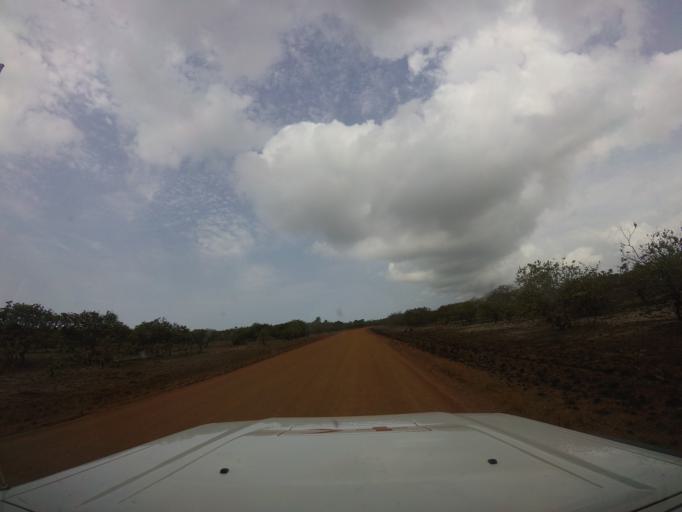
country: LR
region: Grand Cape Mount
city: Robertsport
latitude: 6.6920
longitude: -11.2785
